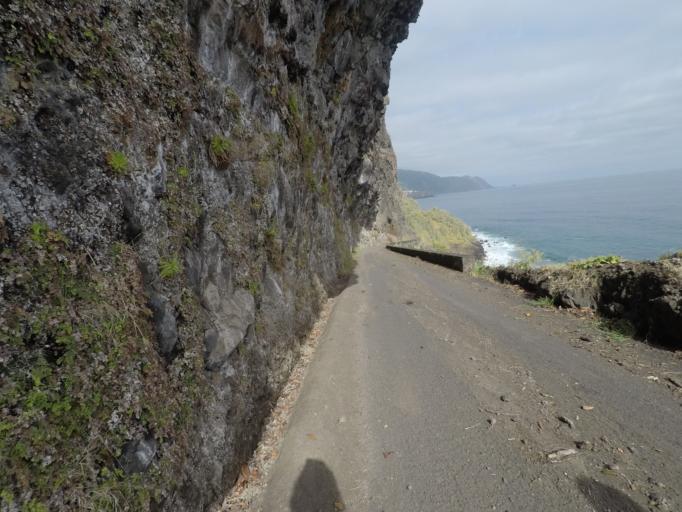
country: PT
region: Madeira
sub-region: Sao Vicente
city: Sao Vicente
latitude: 32.8129
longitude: -17.0685
